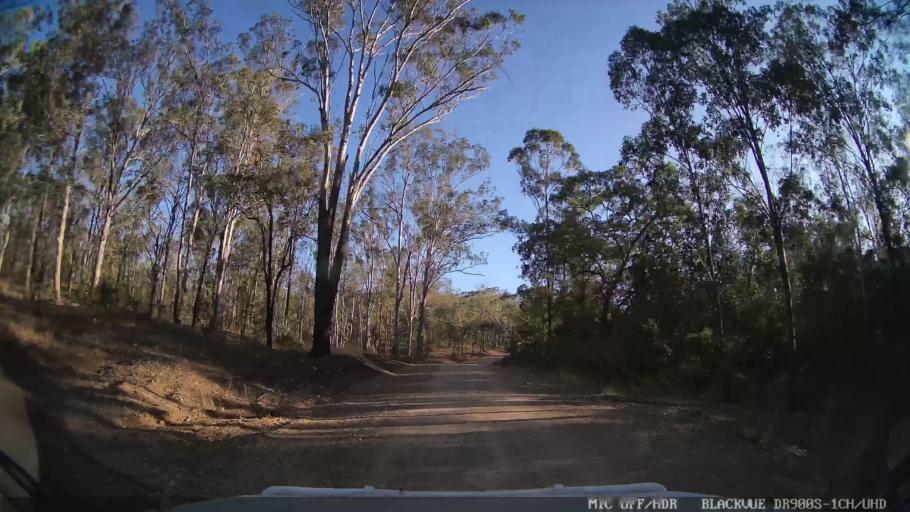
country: AU
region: Queensland
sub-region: Gladstone
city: Toolooa
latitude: -24.6841
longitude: 151.3297
